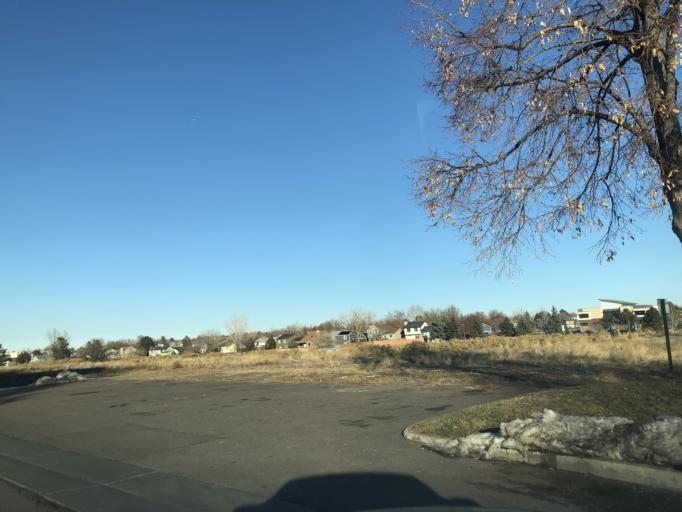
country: US
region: Colorado
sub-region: Adams County
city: Aurora
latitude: 39.7018
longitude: -104.8069
